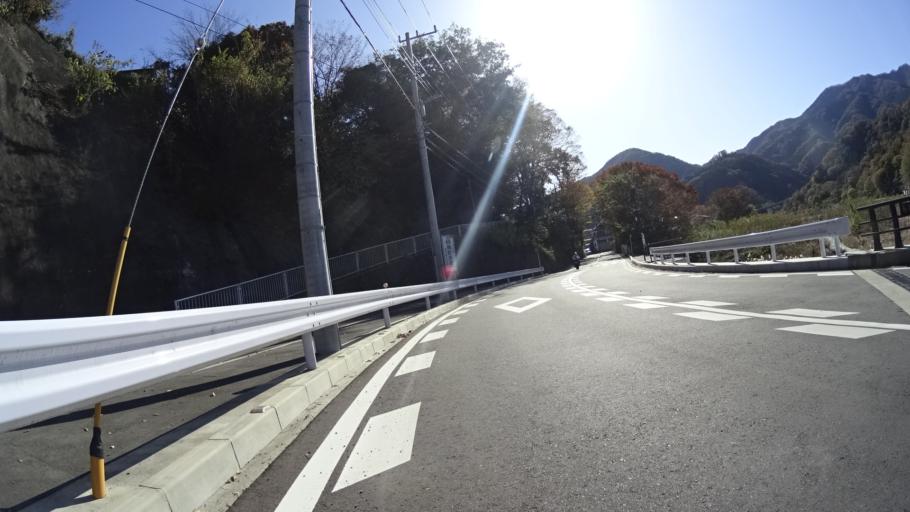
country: JP
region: Kanagawa
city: Zama
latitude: 35.5318
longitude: 139.2856
